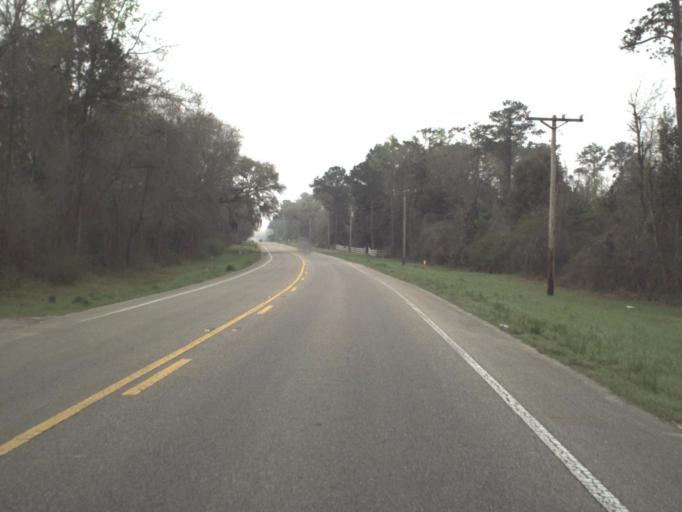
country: US
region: Florida
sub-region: Gadsden County
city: Gretna
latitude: 30.5868
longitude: -84.6723
